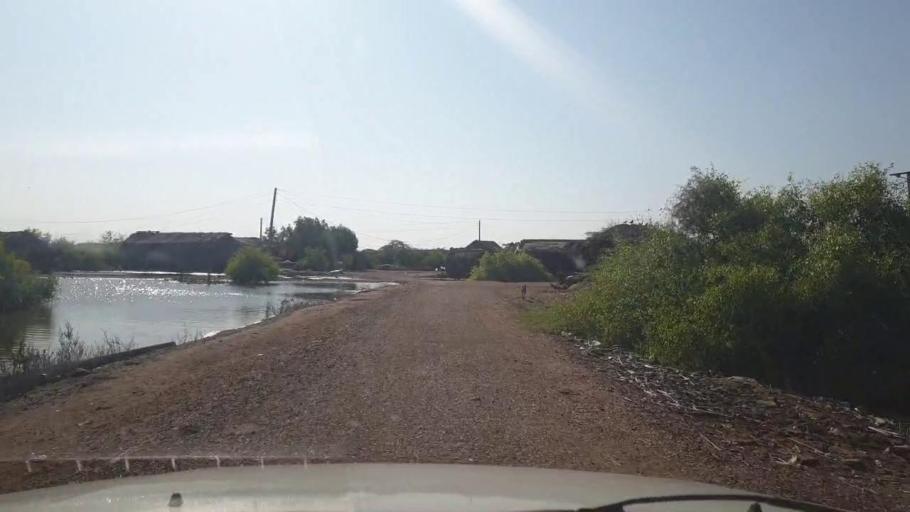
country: PK
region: Sindh
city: Chuhar Jamali
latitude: 24.4619
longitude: 67.9148
